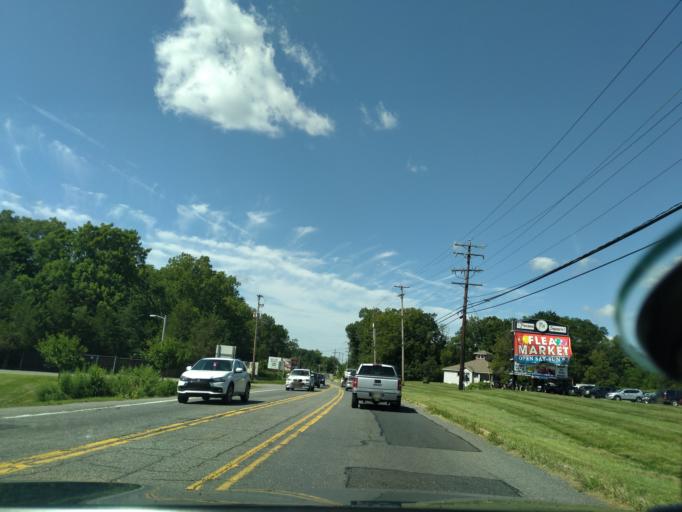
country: US
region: Pennsylvania
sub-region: Pike County
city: Saw Creek
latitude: 41.0624
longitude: -75.0740
